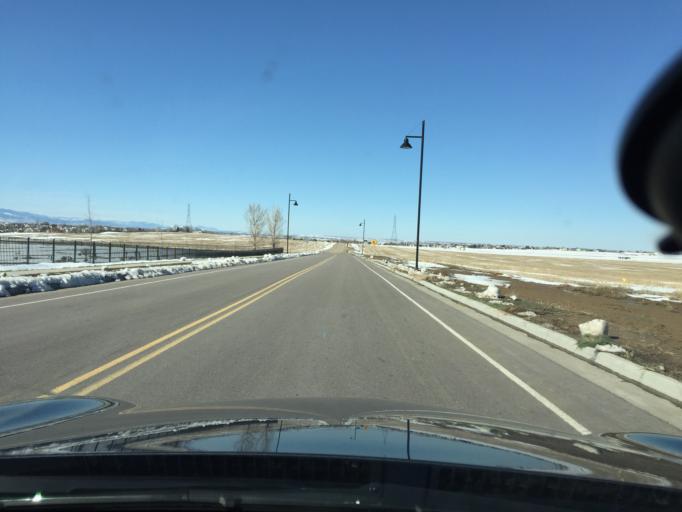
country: US
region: Colorado
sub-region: Boulder County
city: Erie
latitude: 40.0515
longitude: -105.0371
